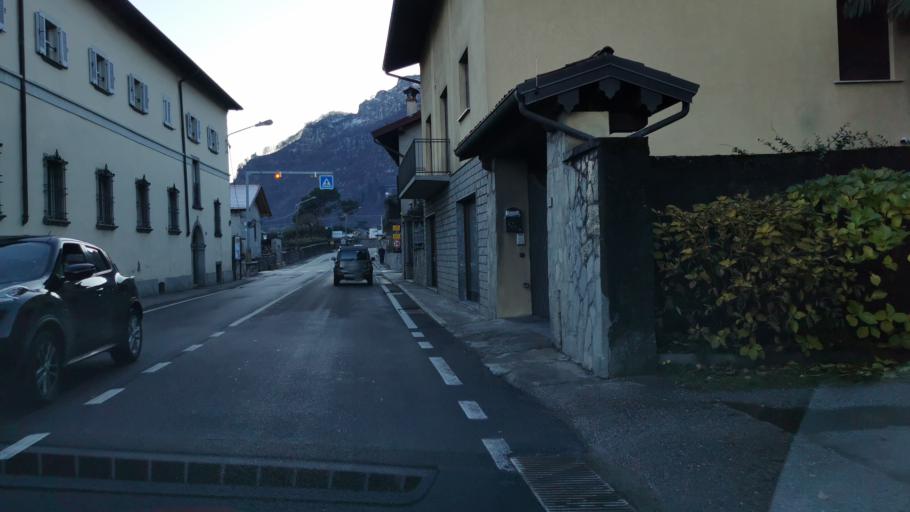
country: IT
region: Lombardy
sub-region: Provincia di Como
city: Dongo
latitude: 46.1285
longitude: 9.2848
